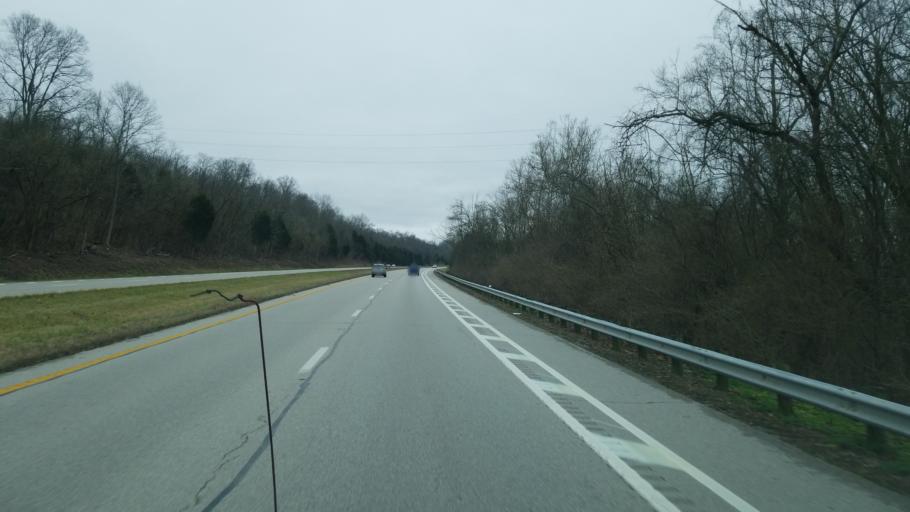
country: US
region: Ohio
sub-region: Clermont County
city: Withamsville
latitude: 39.0066
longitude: -84.3003
